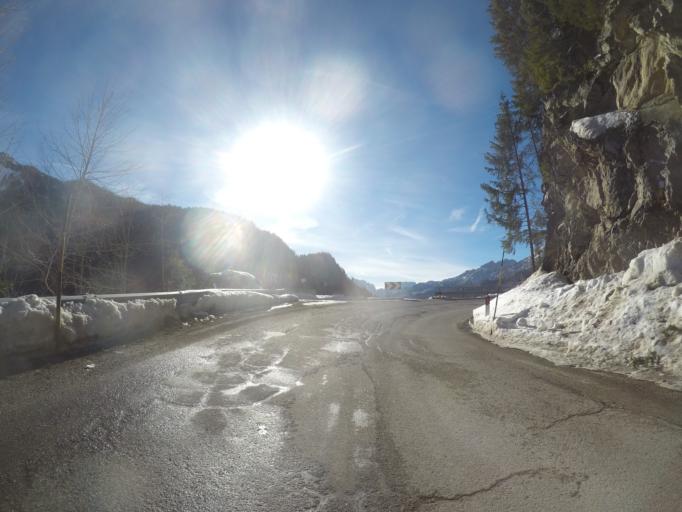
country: IT
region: Veneto
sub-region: Provincia di Belluno
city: Livinallongo del Col di Lana
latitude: 46.4778
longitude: 11.9745
